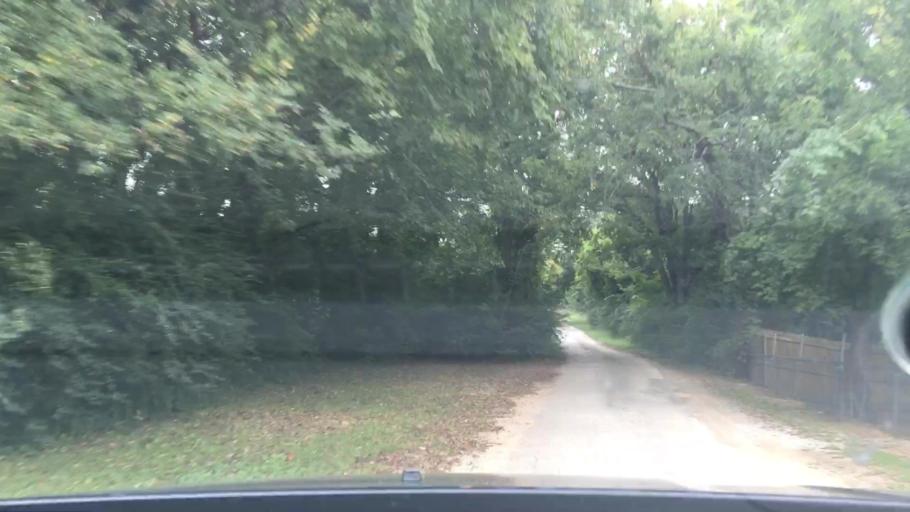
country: US
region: Oklahoma
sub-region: Pontotoc County
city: Ada
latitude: 34.7547
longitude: -96.6480
